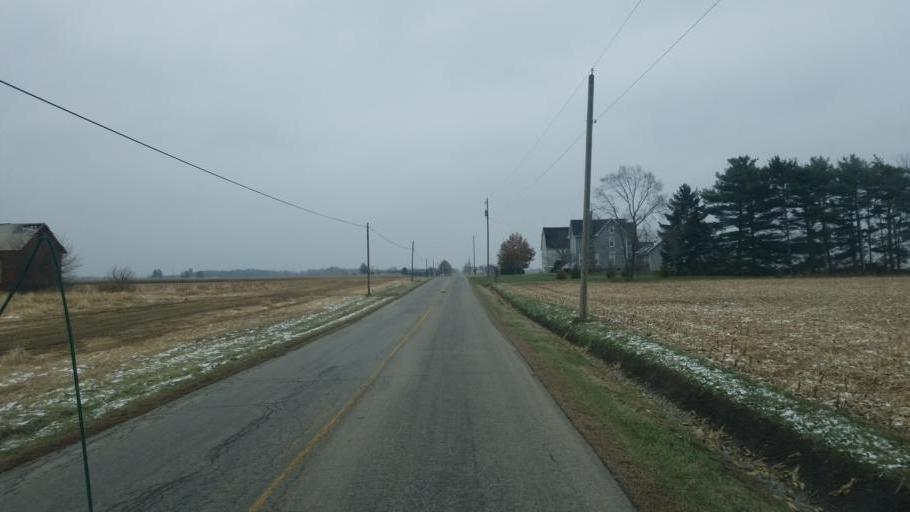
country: US
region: Ohio
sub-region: Richland County
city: Shelby
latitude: 40.9085
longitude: -82.7012
